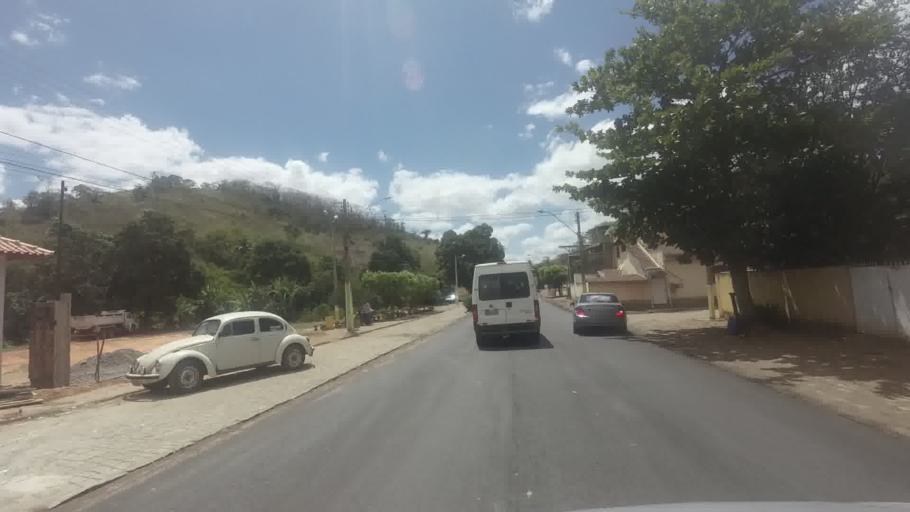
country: BR
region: Rio de Janeiro
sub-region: Santo Antonio De Padua
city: Santo Antonio de Padua
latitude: -21.5026
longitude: -42.0802
